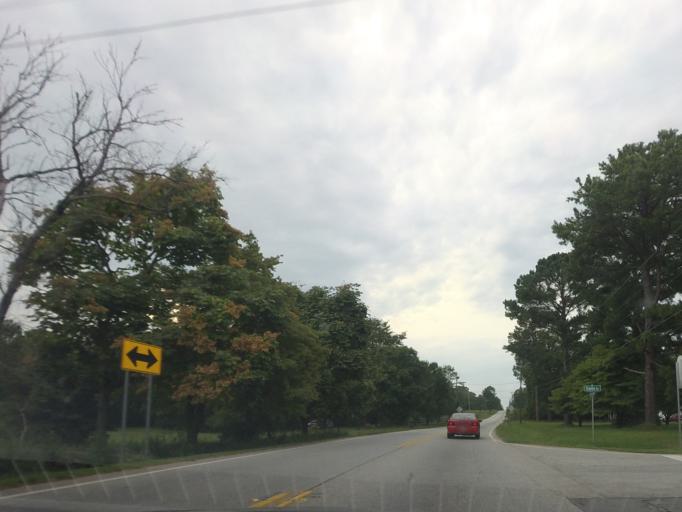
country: US
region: Georgia
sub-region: Bibb County
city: Macon
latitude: 32.8080
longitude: -83.5114
